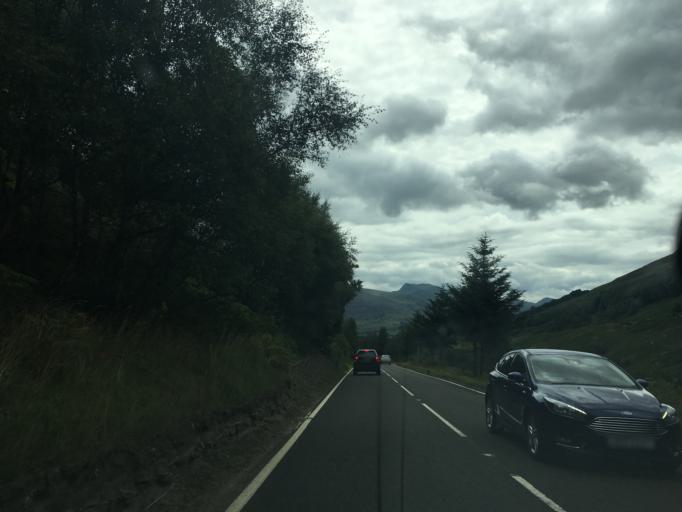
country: GB
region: Scotland
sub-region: Stirling
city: Callander
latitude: 56.4085
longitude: -4.3093
